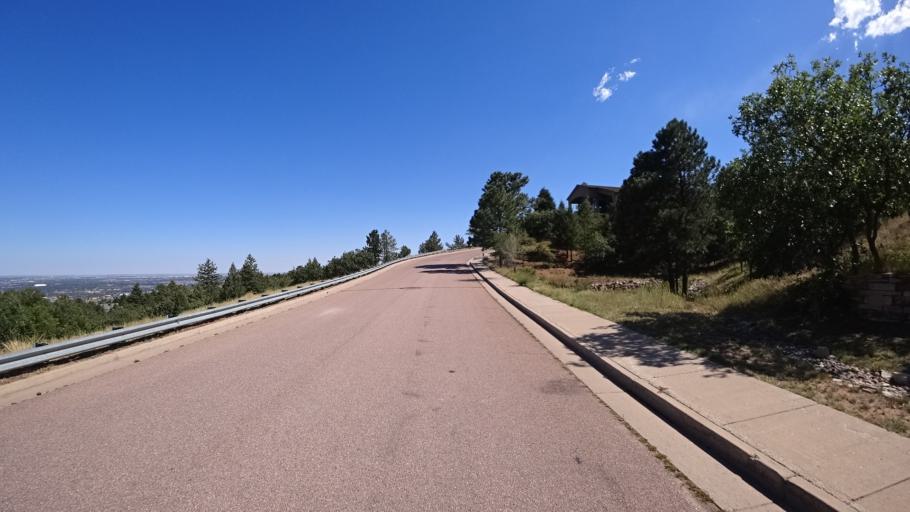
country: US
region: Colorado
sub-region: El Paso County
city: Colorado Springs
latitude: 38.8169
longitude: -104.8753
